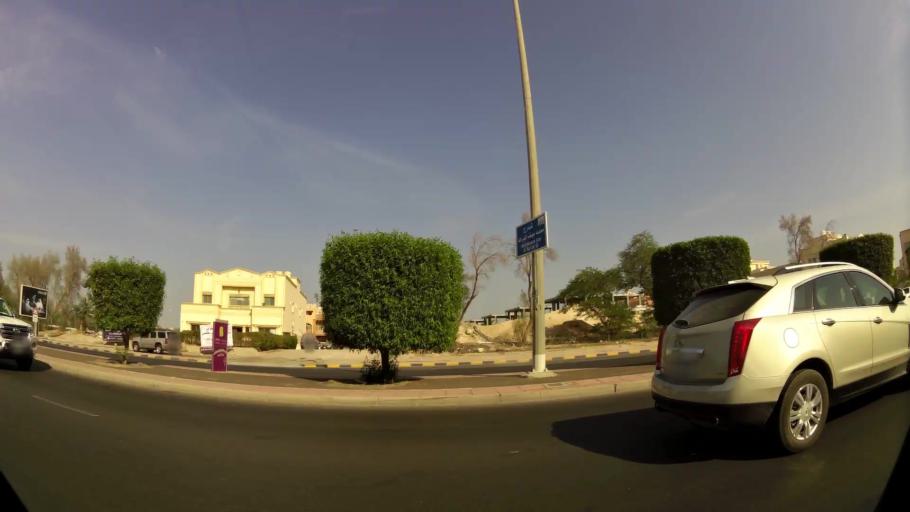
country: KW
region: Al Ahmadi
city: Al Fintas
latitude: 29.1669
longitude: 48.1012
